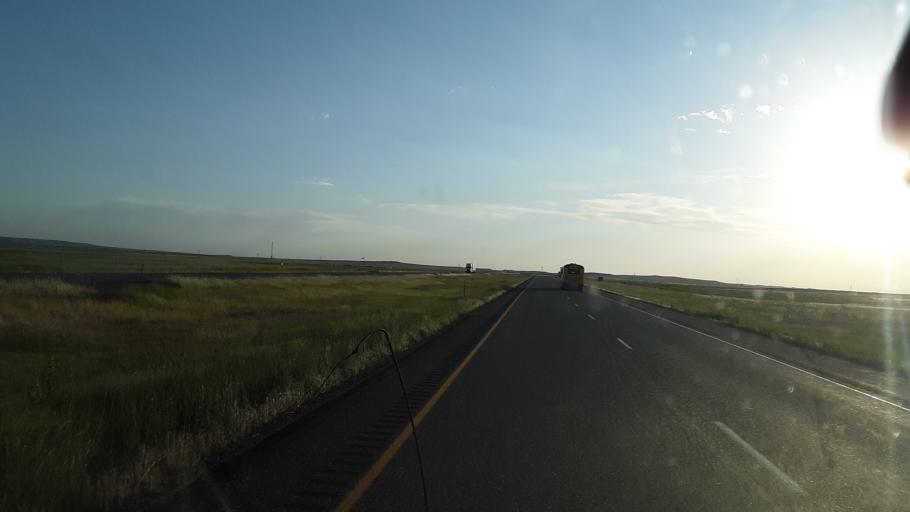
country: US
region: Montana
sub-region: Big Horn County
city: Hardin
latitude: 45.7463
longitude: -107.6562
